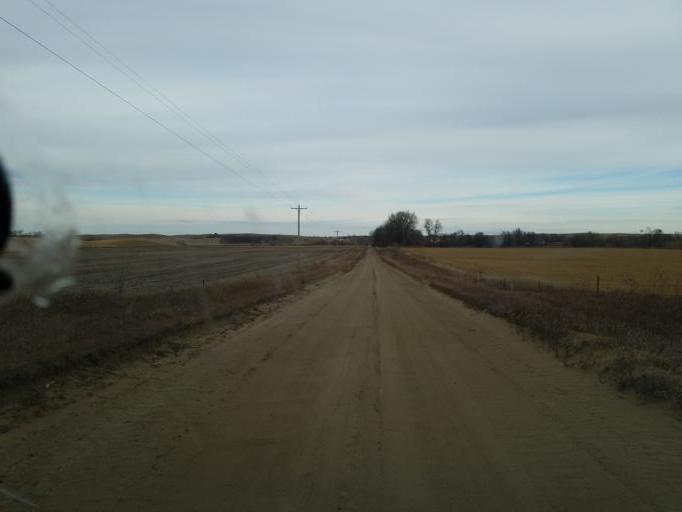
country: US
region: Nebraska
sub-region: Knox County
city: Bloomfield
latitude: 42.5417
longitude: -97.7204
